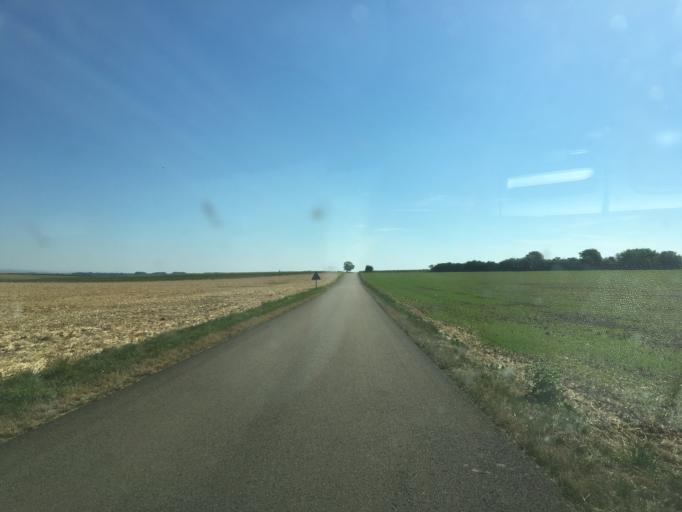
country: FR
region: Bourgogne
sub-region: Departement de l'Yonne
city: Joigny
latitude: 47.9184
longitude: 3.3987
